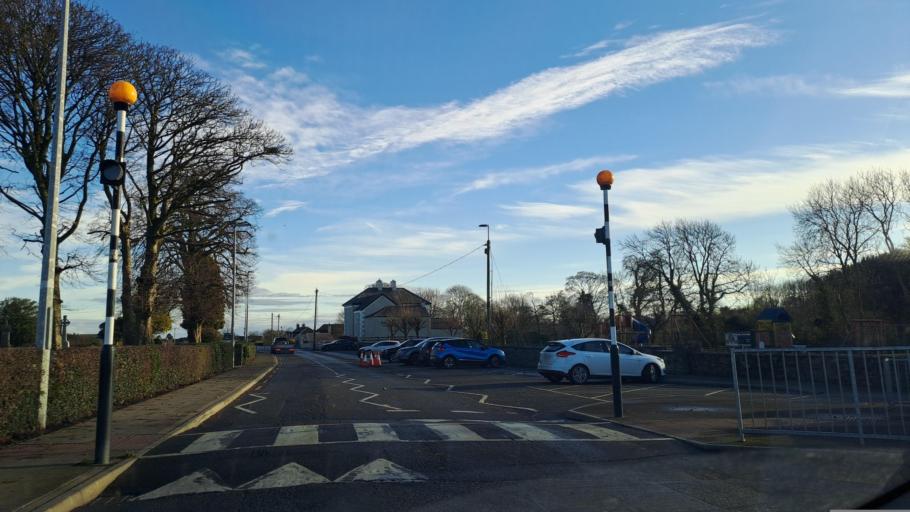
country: IE
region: Ulster
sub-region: An Cabhan
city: Mullagh
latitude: 53.8128
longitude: -6.9573
